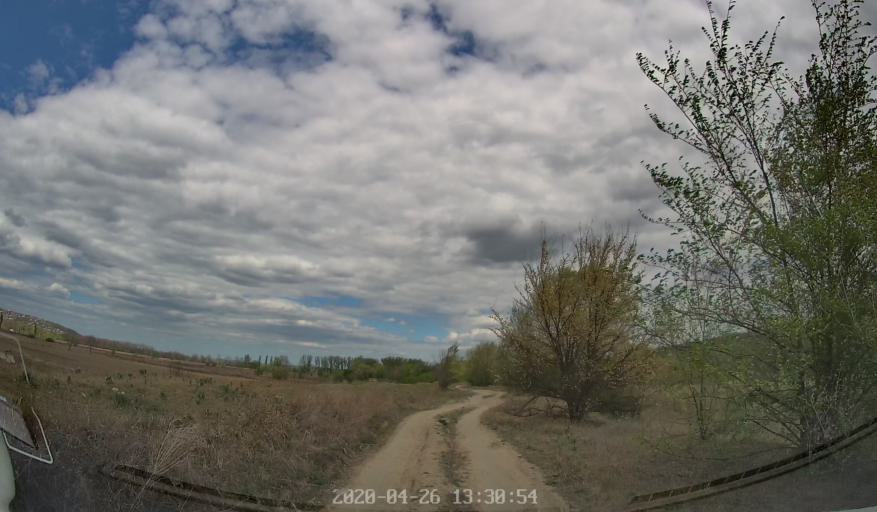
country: MD
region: Criuleni
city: Criuleni
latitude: 47.2065
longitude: 29.1773
